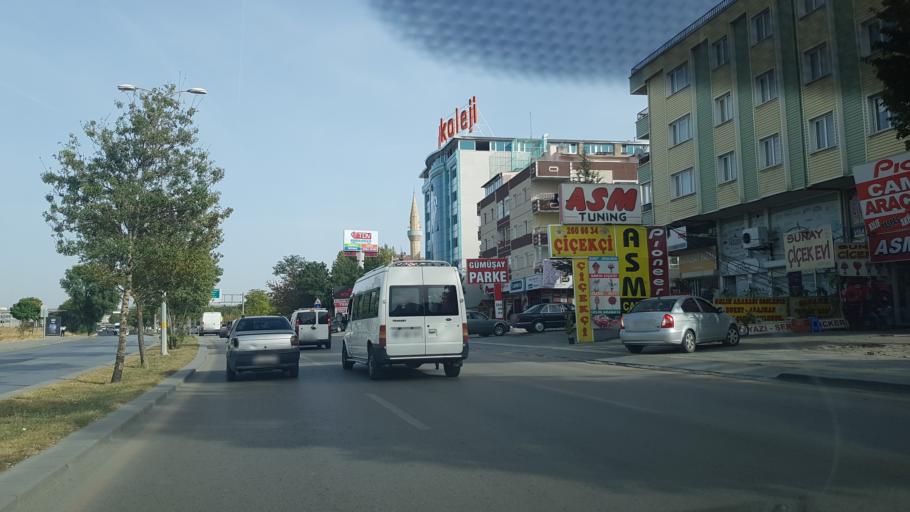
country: TR
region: Ankara
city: Etimesgut
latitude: 39.9567
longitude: 32.6171
